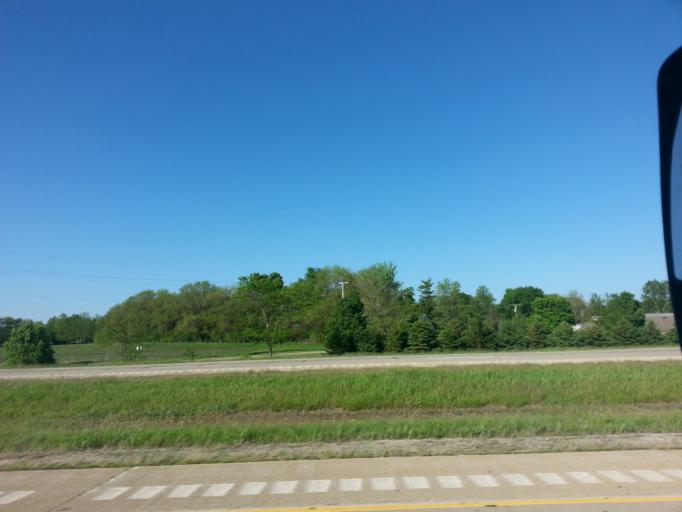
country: US
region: Illinois
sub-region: Marshall County
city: Wenona
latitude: 41.0494
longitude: -89.0629
